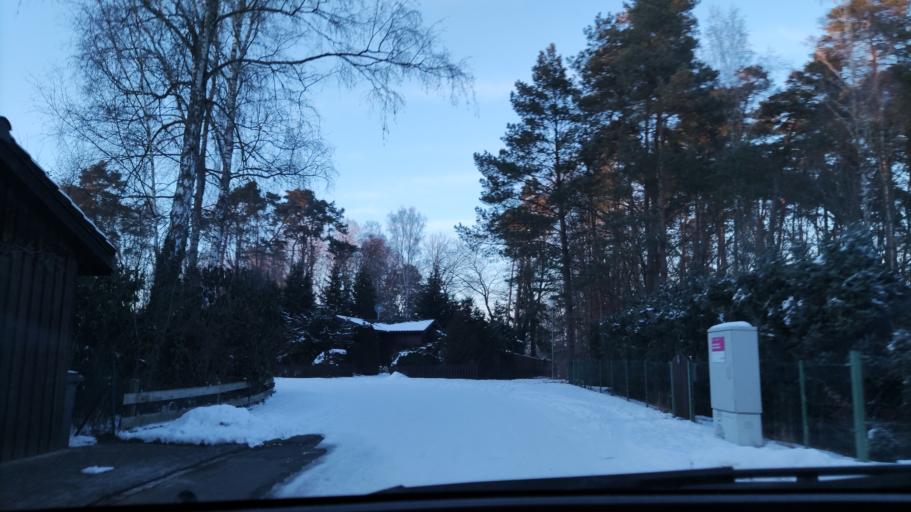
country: DE
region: Lower Saxony
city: Bleckede
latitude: 53.2945
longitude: 10.6910
